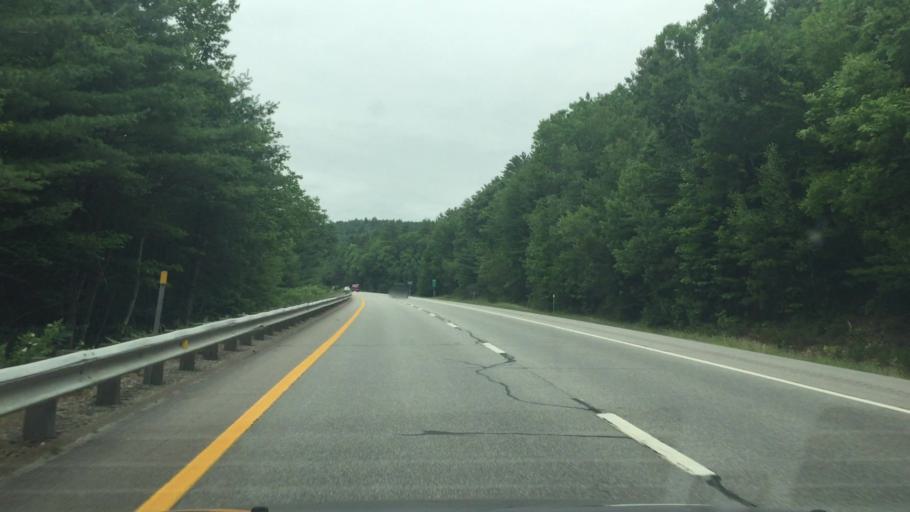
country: US
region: New Hampshire
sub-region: Grafton County
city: Ashland
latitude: 43.5942
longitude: -71.6222
